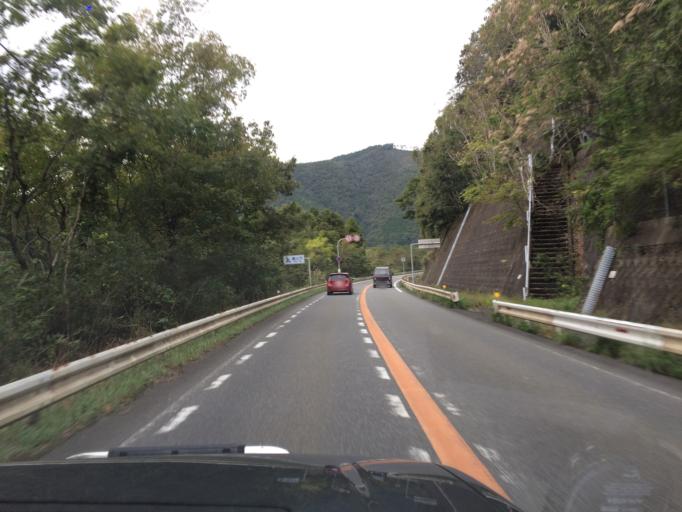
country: JP
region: Hyogo
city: Toyooka
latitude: 35.3695
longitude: 134.8193
